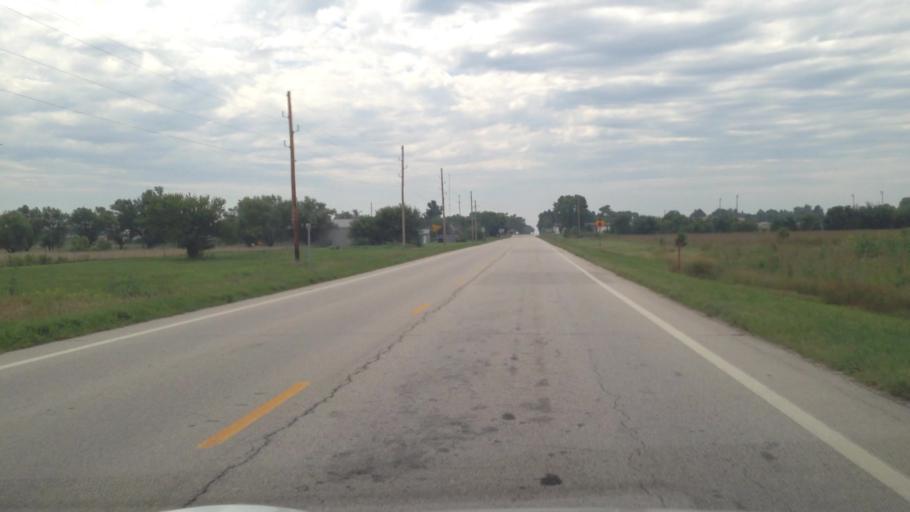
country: US
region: Kansas
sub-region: Allen County
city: Iola
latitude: 37.9261
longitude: -95.1701
